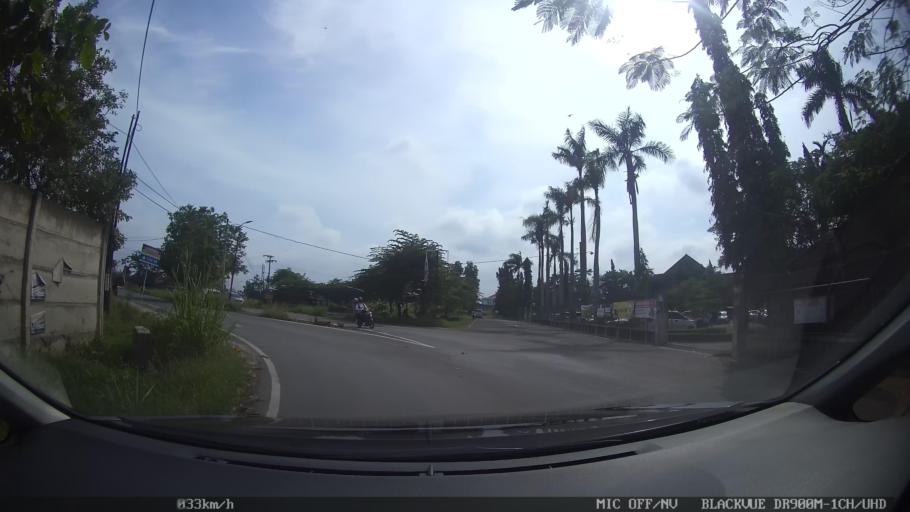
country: ID
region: Lampung
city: Kedaton
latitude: -5.3748
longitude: 105.3082
